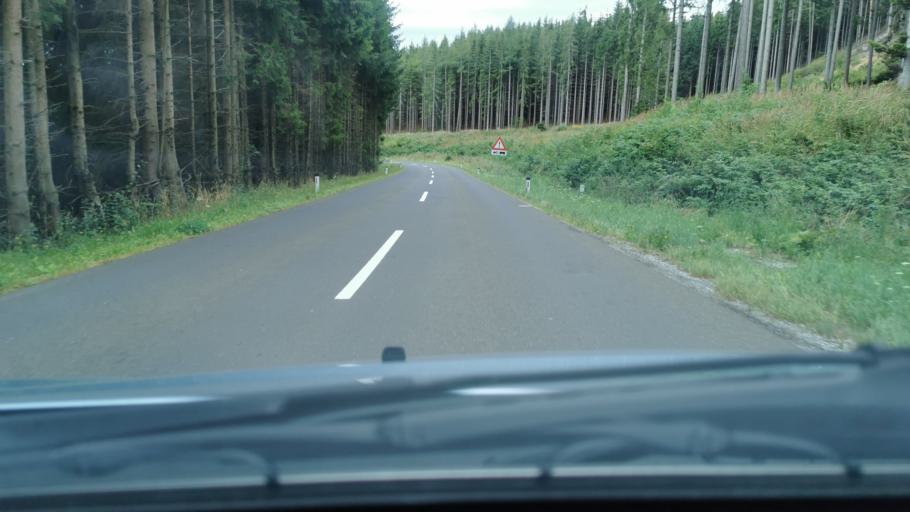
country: AT
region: Styria
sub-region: Politischer Bezirk Weiz
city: Fischbach
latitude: 47.4053
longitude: 15.6631
